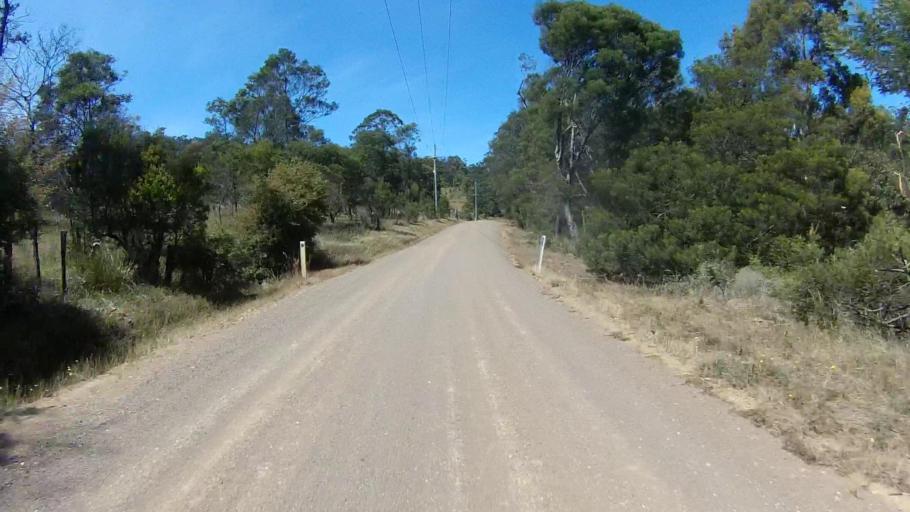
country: AU
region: Tasmania
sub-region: Sorell
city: Sorell
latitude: -42.7675
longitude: 147.6522
